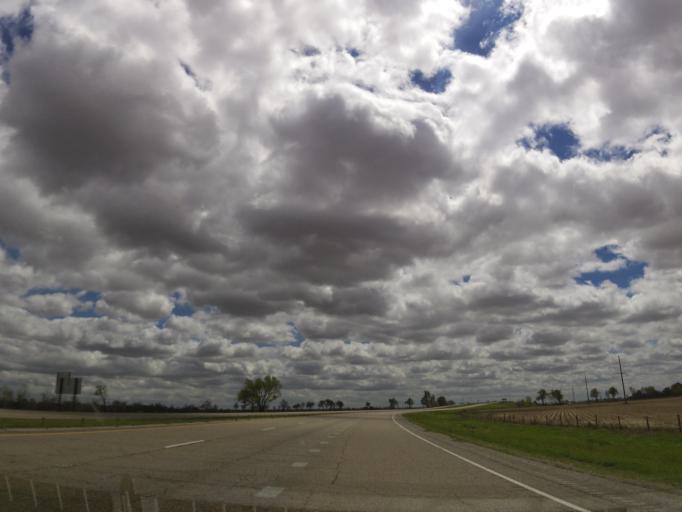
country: US
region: Arkansas
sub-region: Poinsett County
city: Trumann
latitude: 35.6267
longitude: -90.4979
